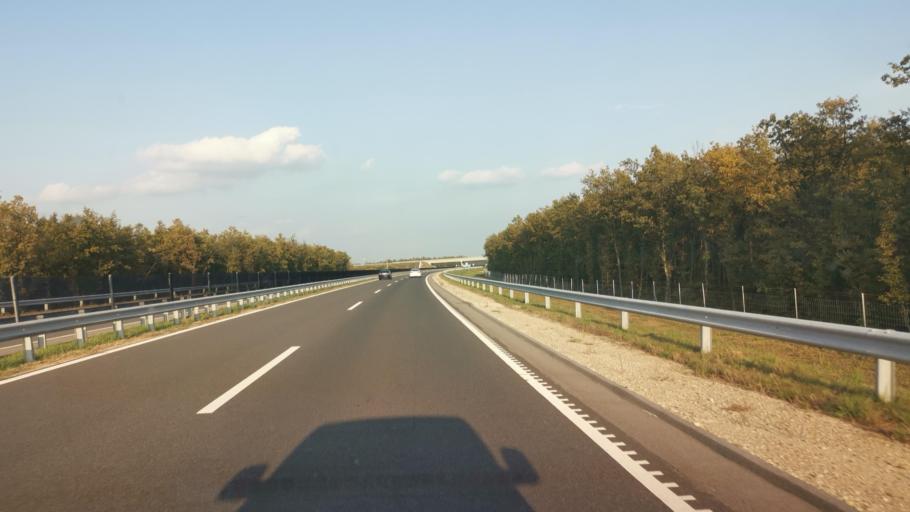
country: HU
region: Gyor-Moson-Sopron
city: Fertoszentmiklos
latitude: 47.5838
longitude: 16.9279
